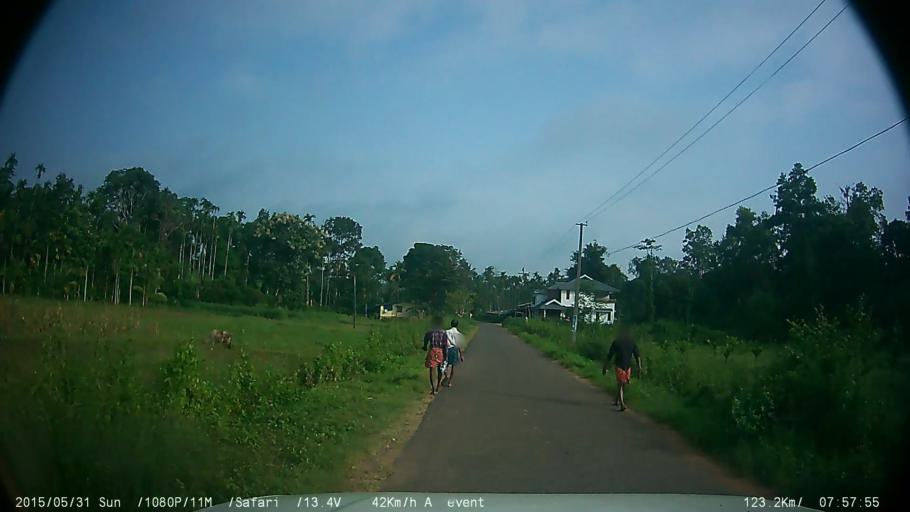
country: IN
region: Kerala
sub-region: Wayanad
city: Kalpetta
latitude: 11.6331
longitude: 76.0639
